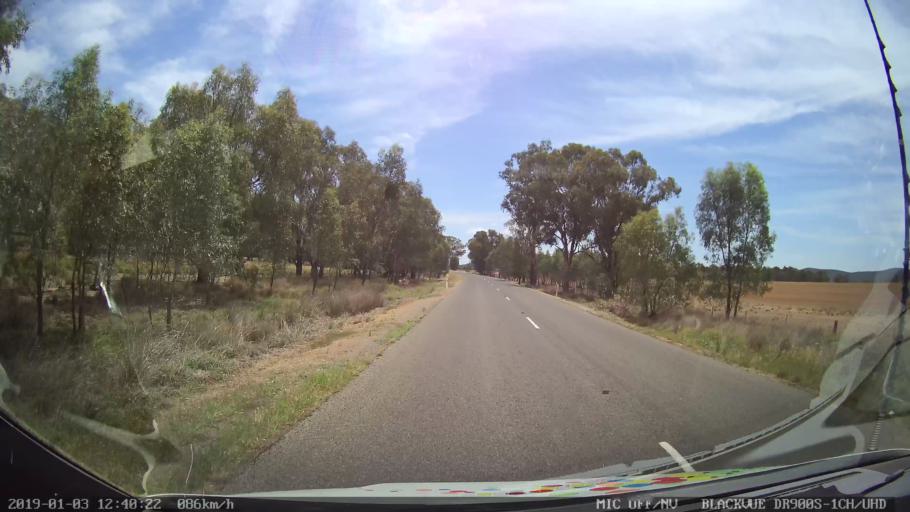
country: AU
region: New South Wales
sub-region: Weddin
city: Grenfell
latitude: -33.8133
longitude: 148.2118
